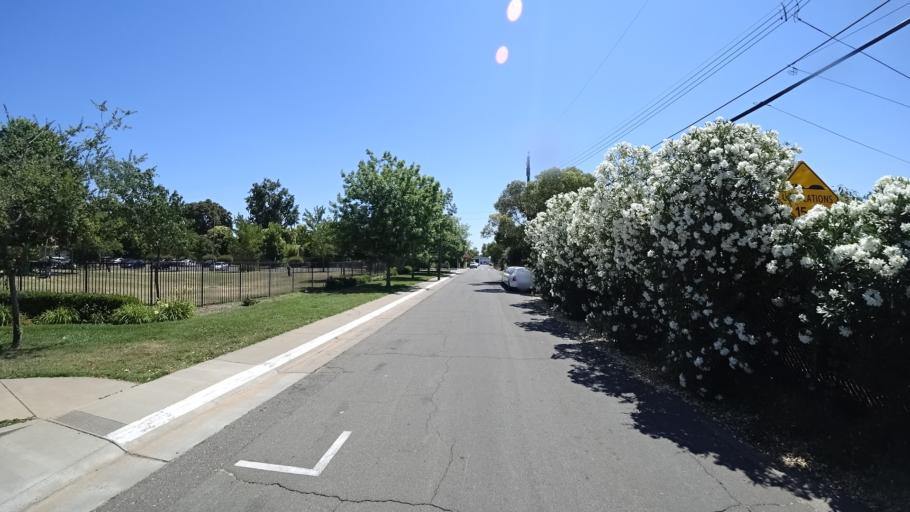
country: US
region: California
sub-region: Sacramento County
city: Parkway
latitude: 38.5380
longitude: -121.4779
